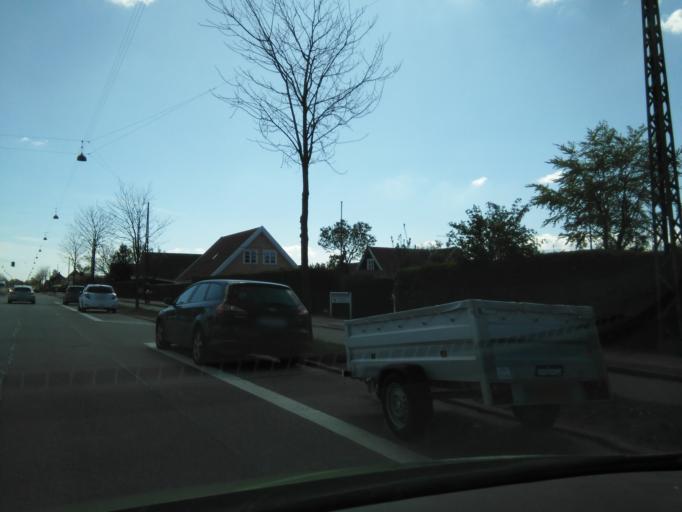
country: DK
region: Capital Region
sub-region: Tarnby Kommune
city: Tarnby
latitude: 55.6472
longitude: 12.5980
